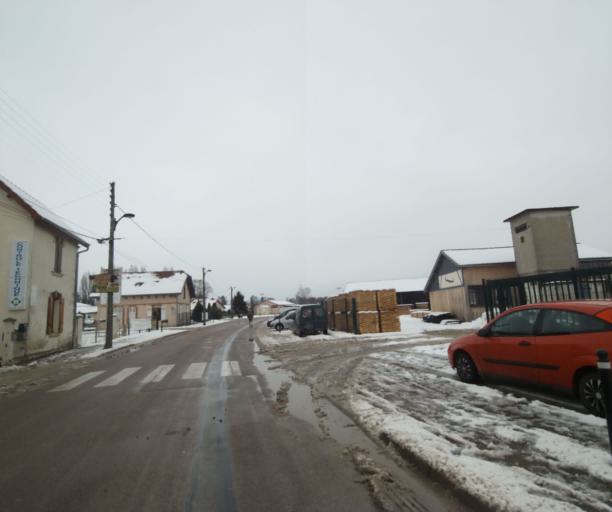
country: FR
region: Champagne-Ardenne
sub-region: Departement de la Haute-Marne
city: Montier-en-Der
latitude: 48.4745
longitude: 4.7733
